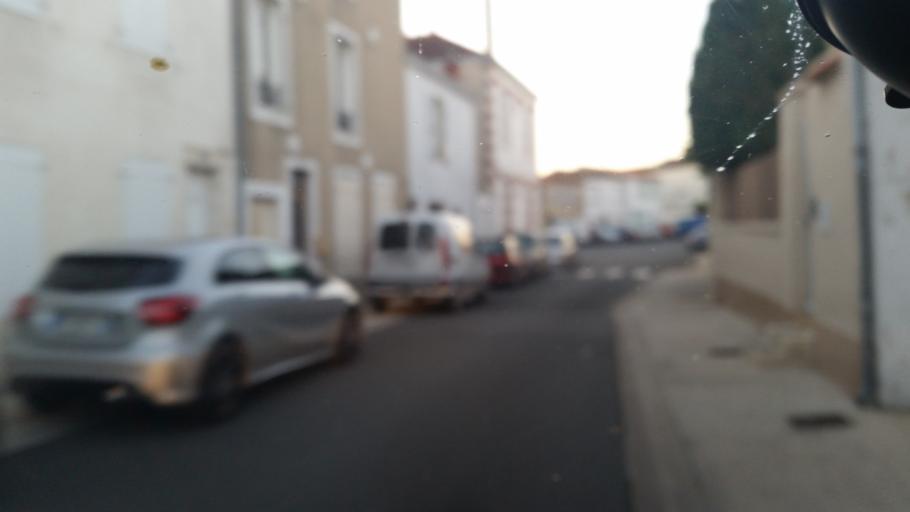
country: FR
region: Poitou-Charentes
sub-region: Departement de la Charente-Maritime
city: Marans
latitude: 46.3109
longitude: -0.9953
